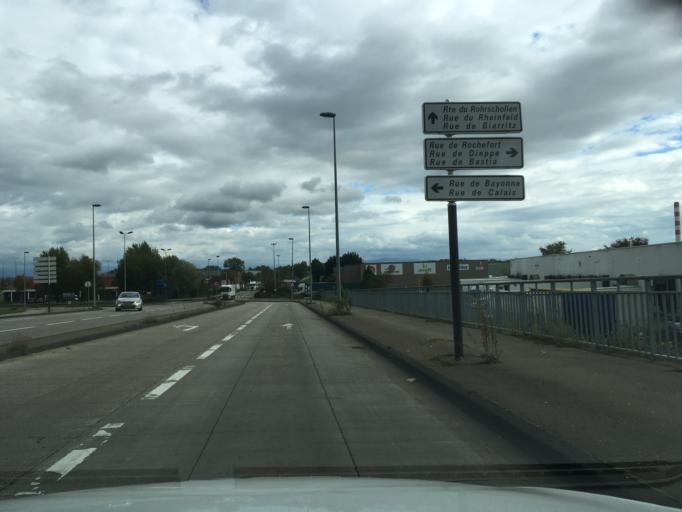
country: DE
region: Baden-Wuerttemberg
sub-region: Freiburg Region
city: Kehl
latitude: 48.5246
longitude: 7.7798
